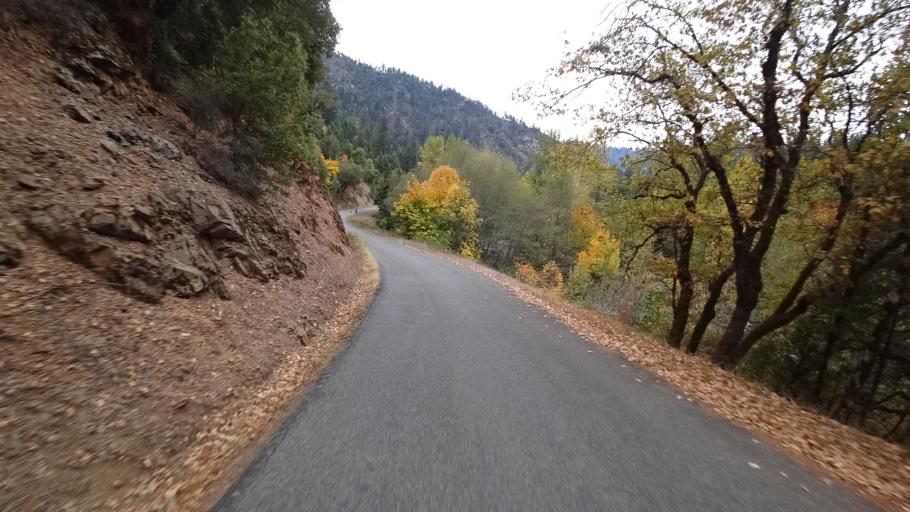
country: US
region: California
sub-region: Siskiyou County
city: Happy Camp
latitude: 41.7502
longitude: -123.3605
